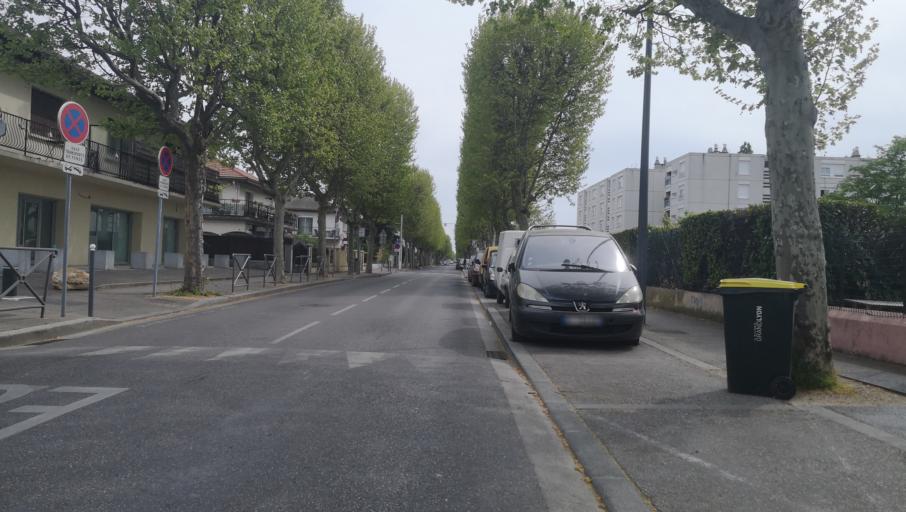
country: FR
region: Rhone-Alpes
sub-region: Departement du Rhone
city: Bron
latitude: 45.7562
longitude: 4.9284
